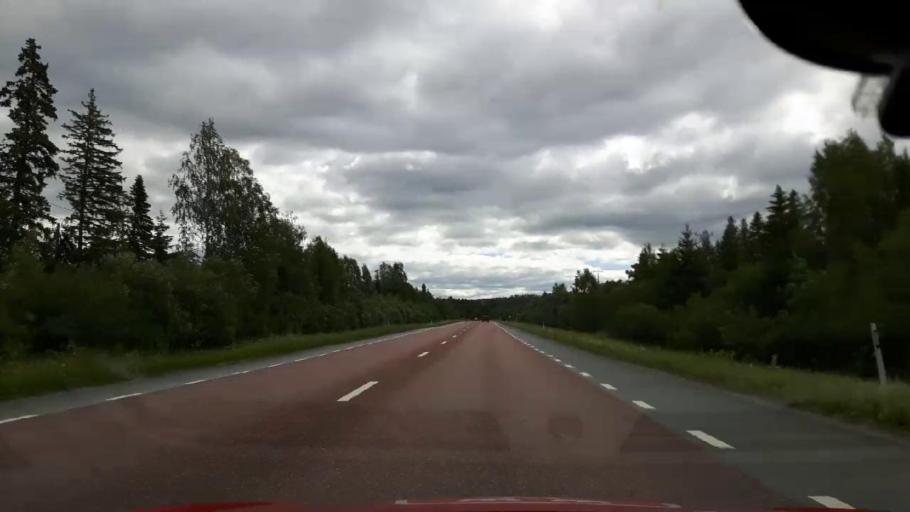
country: SE
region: Jaemtland
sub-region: Braecke Kommun
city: Braecke
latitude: 62.8176
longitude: 15.3394
